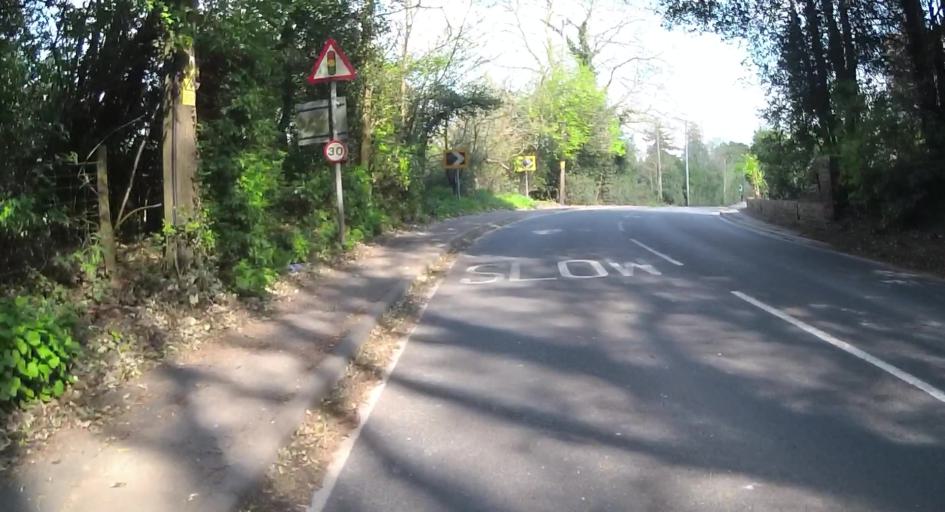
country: GB
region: England
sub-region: West Berkshire
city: Stratfield Mortimer
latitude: 51.3754
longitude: -1.0519
